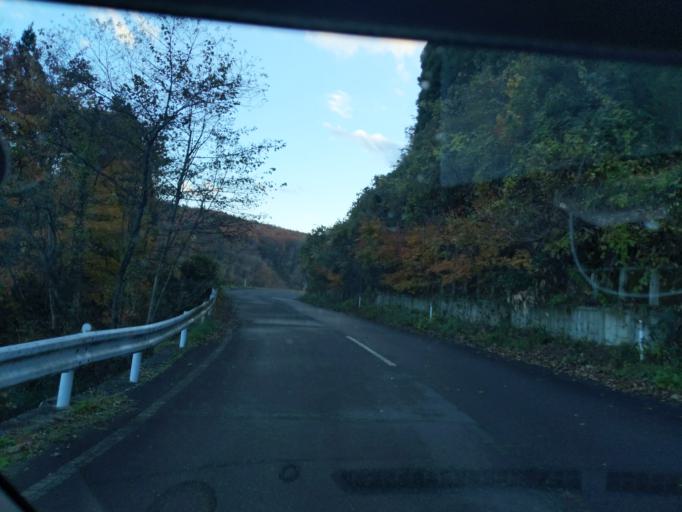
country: JP
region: Iwate
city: Mizusawa
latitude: 39.0297
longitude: 141.0376
